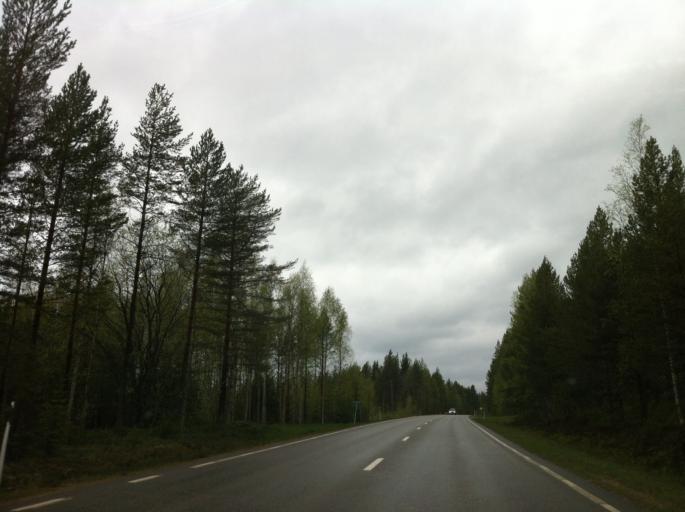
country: SE
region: Jaemtland
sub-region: Harjedalens Kommun
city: Sveg
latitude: 62.0475
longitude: 14.3283
